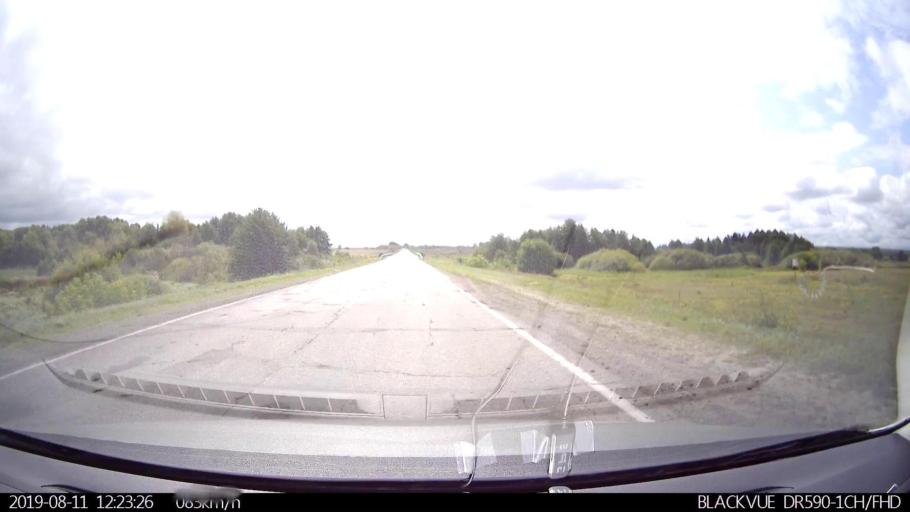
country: RU
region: Ulyanovsk
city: Ignatovka
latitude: 53.8954
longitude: 47.9504
